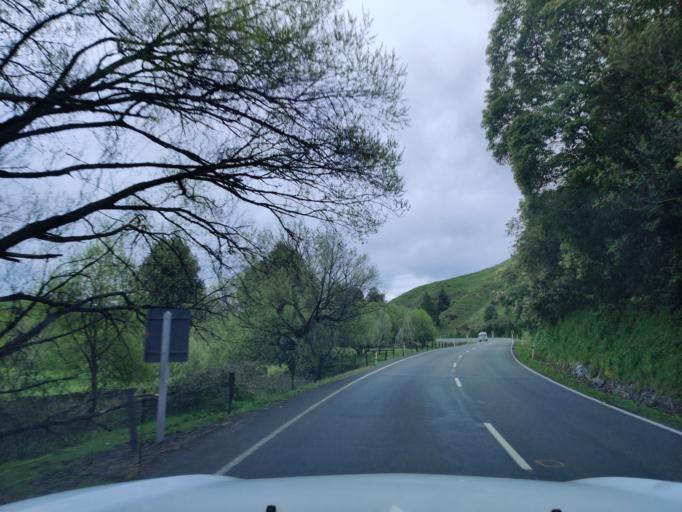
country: NZ
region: Waikato
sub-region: Otorohanga District
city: Otorohanga
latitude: -38.4857
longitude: 175.1804
